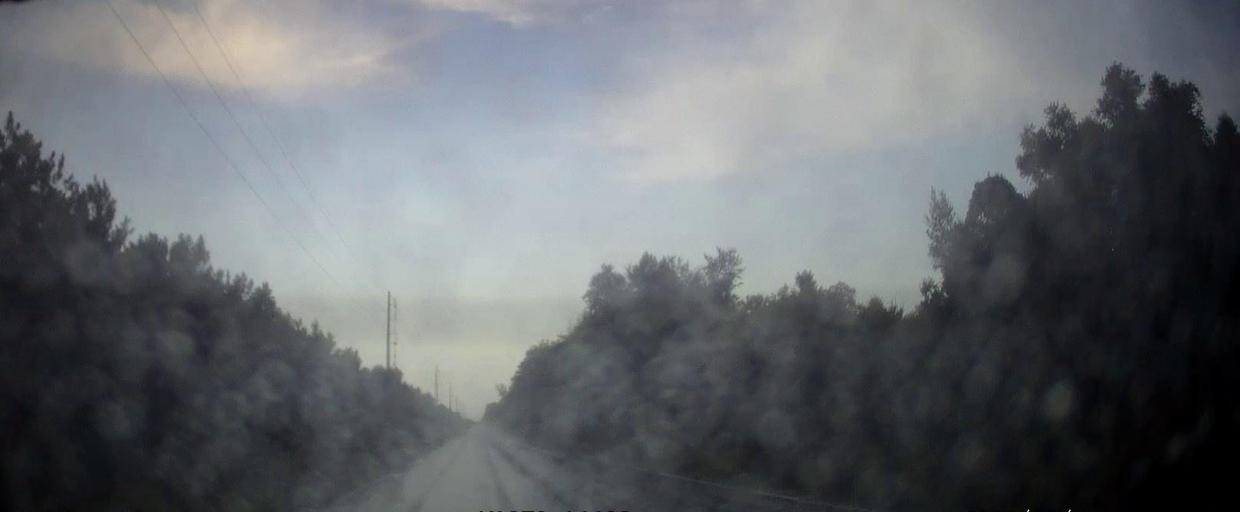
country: US
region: Georgia
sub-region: Dodge County
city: Chester
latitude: 32.5678
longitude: -83.1799
